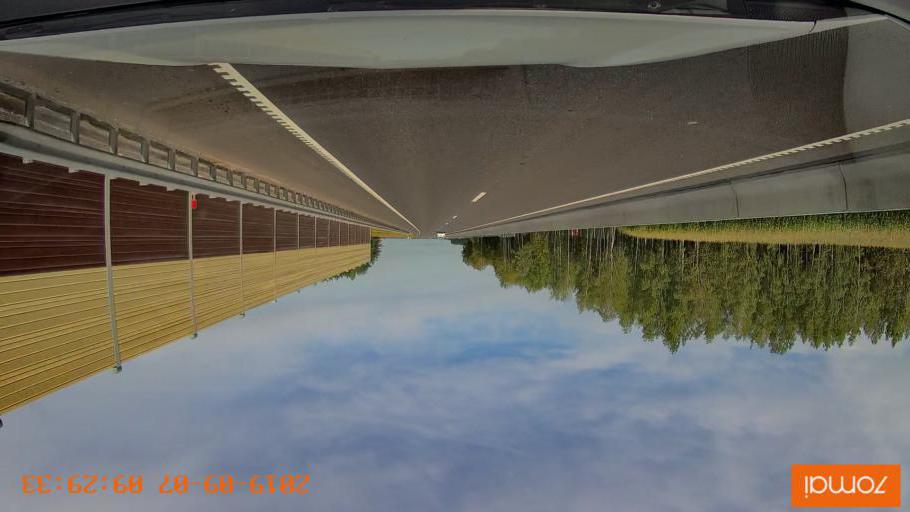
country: BY
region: Grodnenskaya
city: Lyubcha
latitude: 53.9091
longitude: 26.0159
